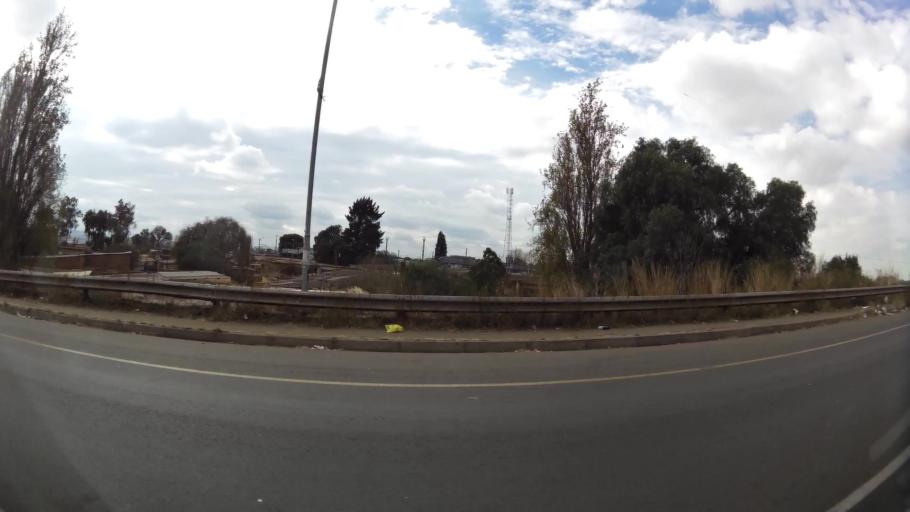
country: ZA
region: Gauteng
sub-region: City of Johannesburg Metropolitan Municipality
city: Soweto
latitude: -26.2736
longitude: 27.8865
